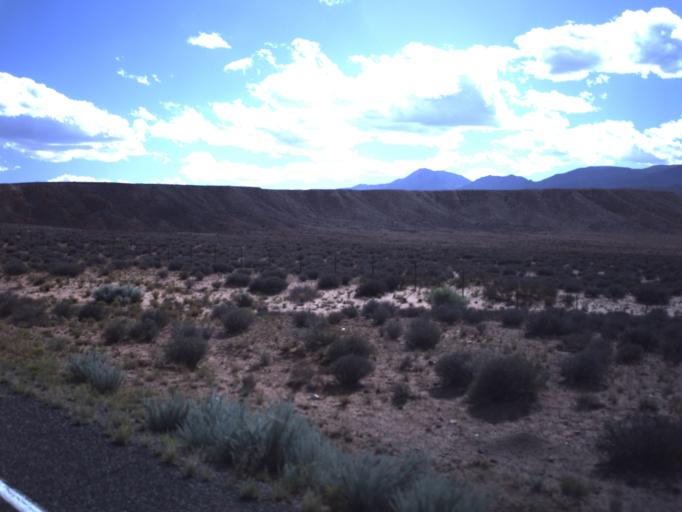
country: US
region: Utah
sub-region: Wayne County
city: Loa
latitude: 38.1534
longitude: -110.6207
